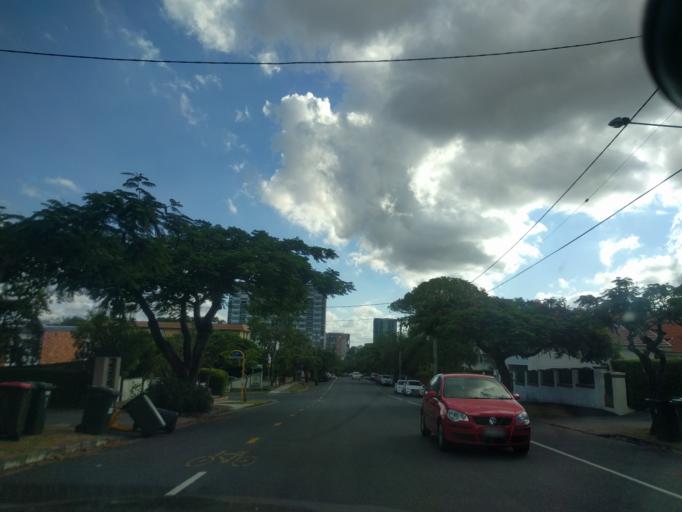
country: AU
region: Queensland
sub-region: Brisbane
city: Brisbane
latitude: -27.4723
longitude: 153.0444
